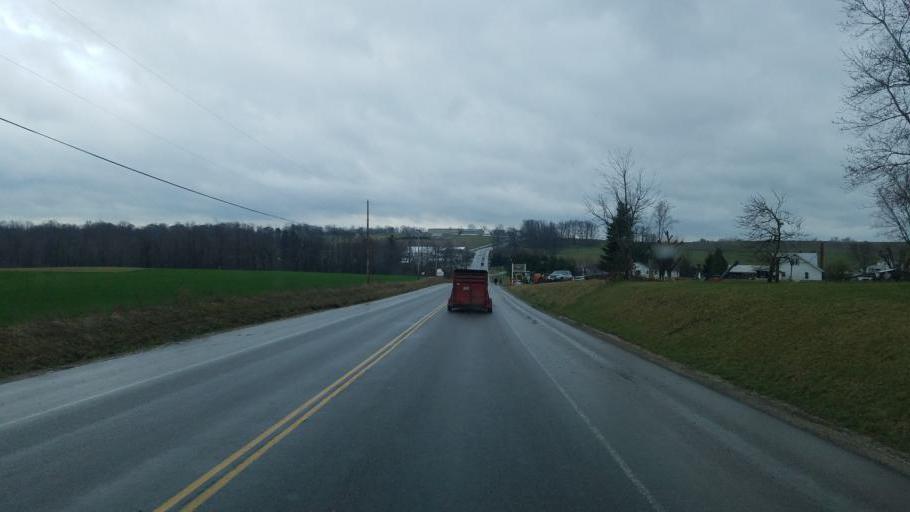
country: US
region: Ohio
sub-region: Wayne County
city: Apple Creek
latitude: 40.6177
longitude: -81.7835
